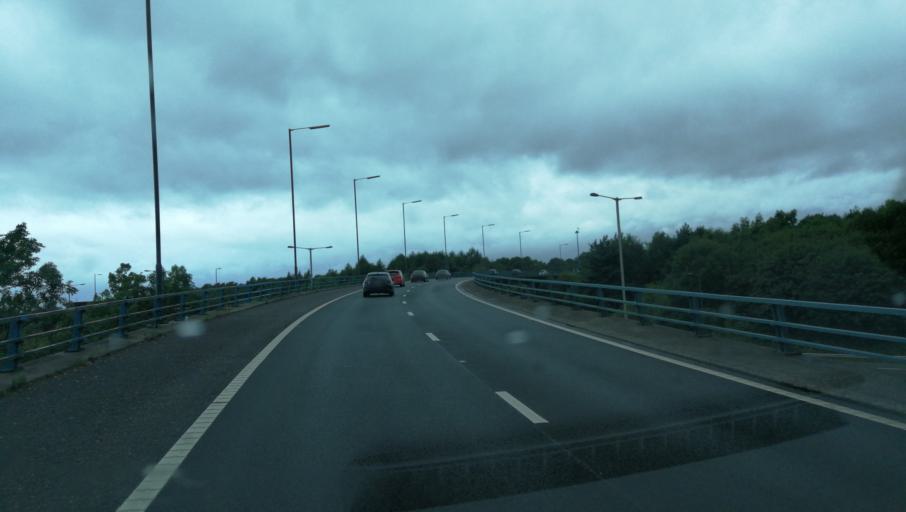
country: GB
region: England
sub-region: Manchester
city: Swinton
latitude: 53.5238
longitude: -2.3590
